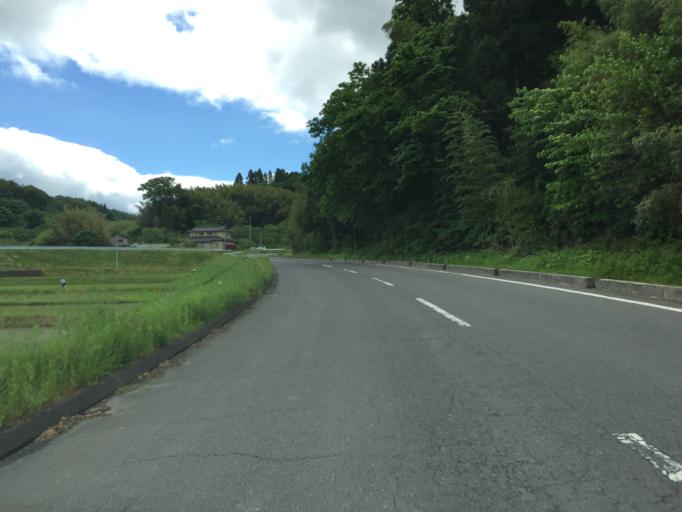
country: JP
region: Fukushima
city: Miharu
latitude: 37.4940
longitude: 140.4625
